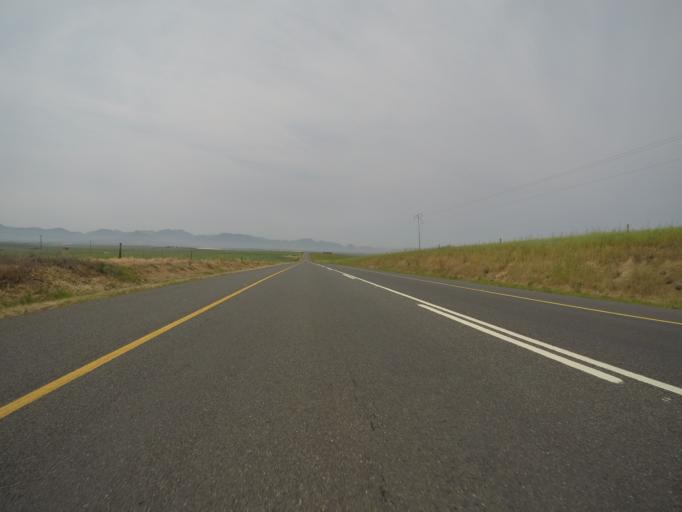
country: ZA
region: Western Cape
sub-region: West Coast District Municipality
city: Malmesbury
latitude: -33.5451
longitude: 18.8632
